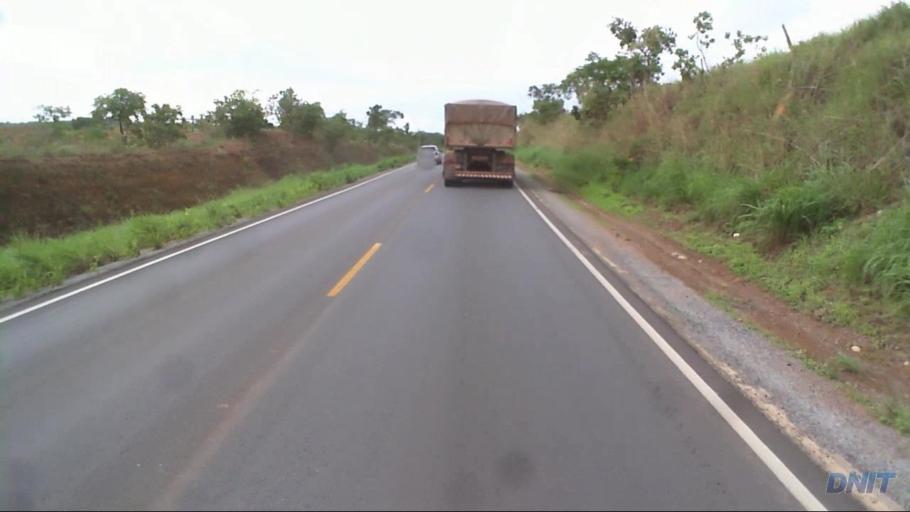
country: BR
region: Goias
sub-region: Padre Bernardo
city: Padre Bernardo
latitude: -15.1906
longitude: -48.2843
